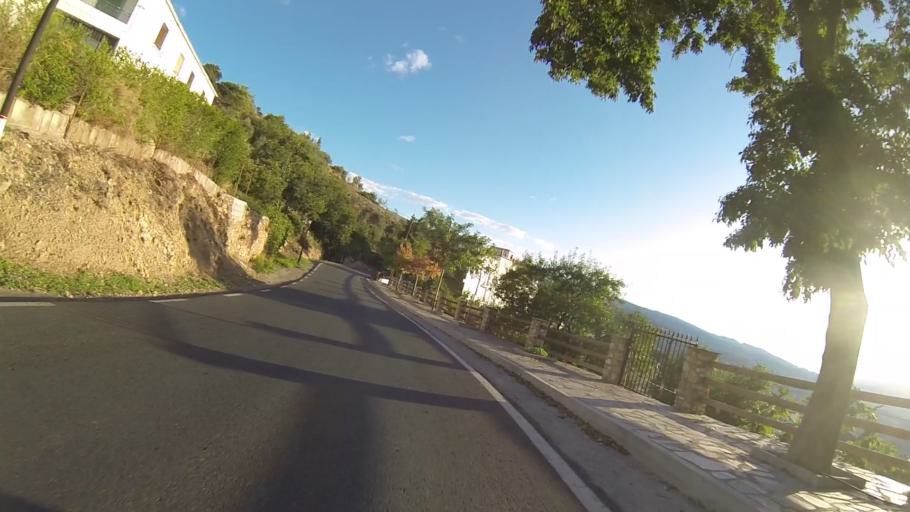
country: ES
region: Andalusia
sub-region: Provincia de Granada
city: Valor
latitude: 36.9824
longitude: -3.1205
